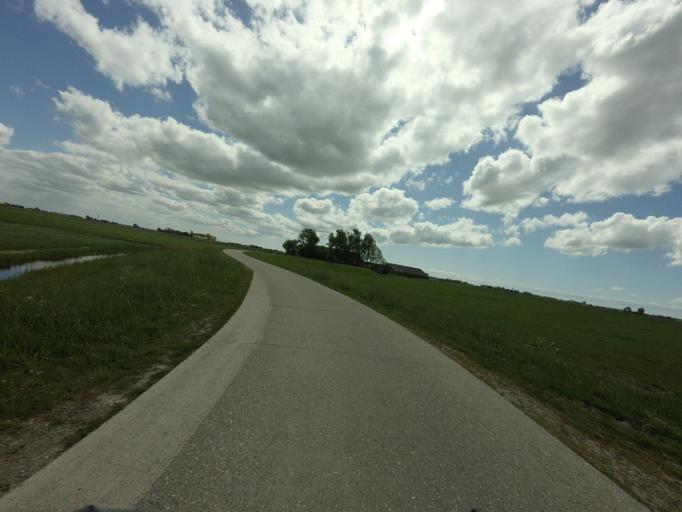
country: NL
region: Friesland
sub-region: Gemeente Littenseradiel
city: Wommels
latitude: 53.1210
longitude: 5.5533
